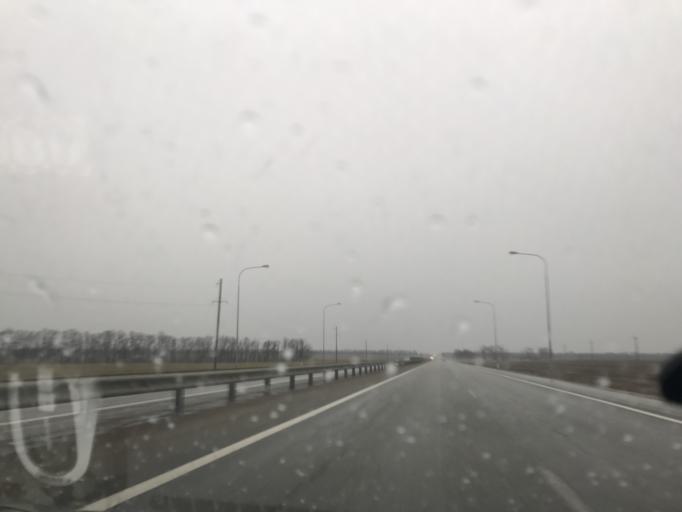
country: RU
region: Krasnodarskiy
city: Kislyakovskaya
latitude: 46.3327
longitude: 39.7875
